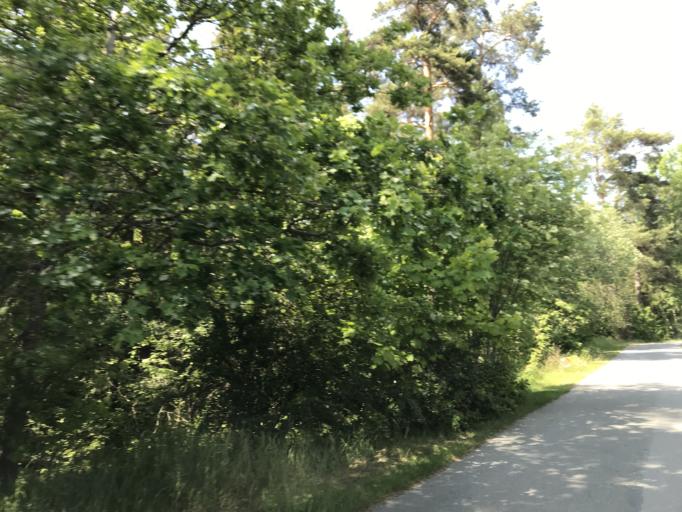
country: SE
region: Stockholm
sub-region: Upplands Vasby Kommun
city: Upplands Vaesby
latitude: 59.4637
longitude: 17.9011
